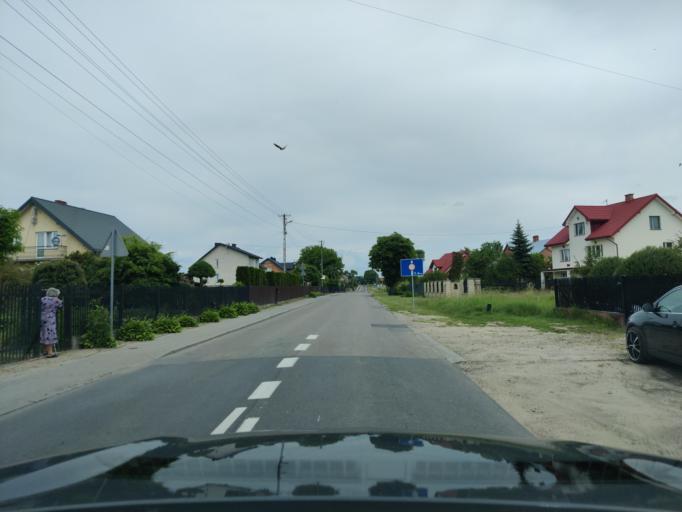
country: PL
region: Masovian Voivodeship
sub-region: Powiat wyszkowski
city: Rzasnik
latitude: 52.6837
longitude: 21.4177
